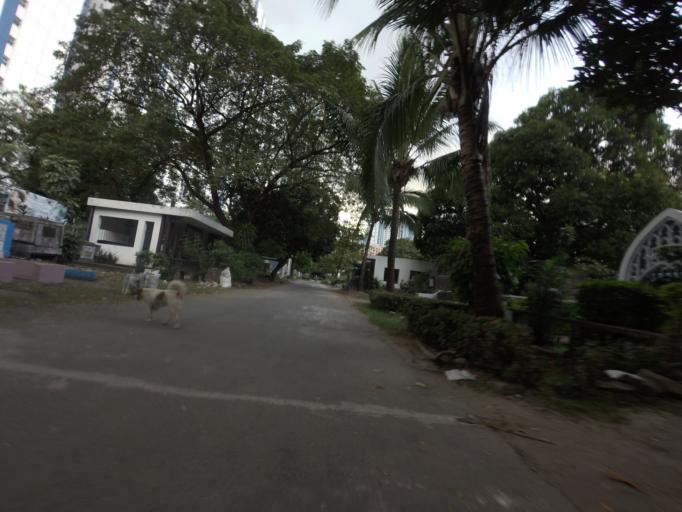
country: PH
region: Metro Manila
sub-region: Makati City
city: Makati City
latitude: 14.5649
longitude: 121.0212
